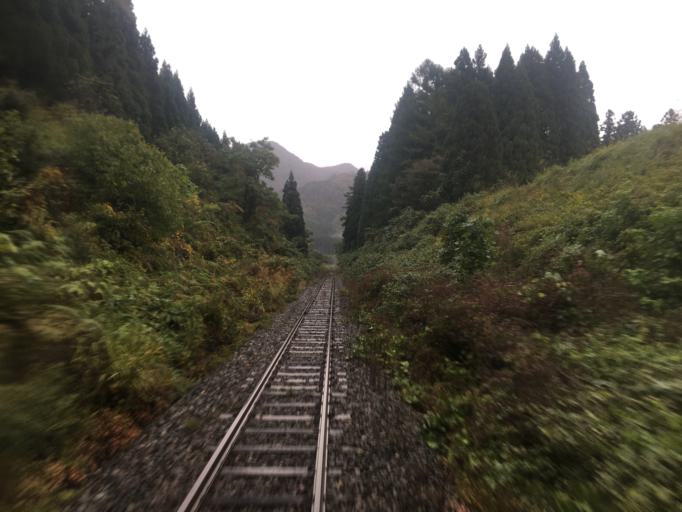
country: JP
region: Yamagata
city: Shinjo
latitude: 38.7222
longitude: 140.3861
